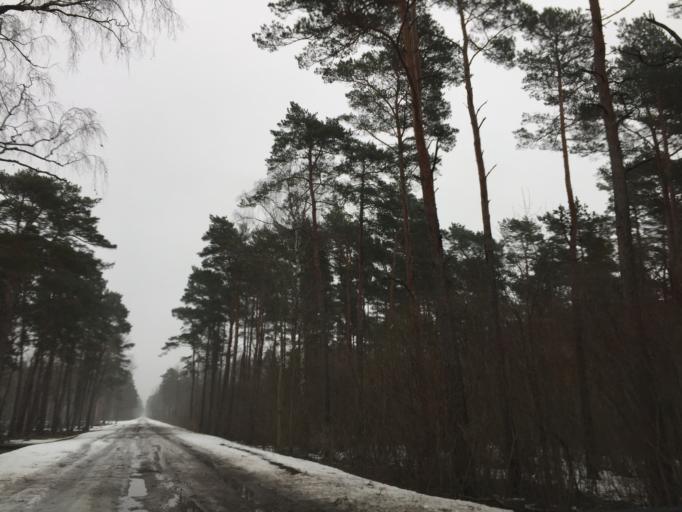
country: EE
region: Saare
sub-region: Kuressaare linn
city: Kuressaare
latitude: 58.2670
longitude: 22.5389
